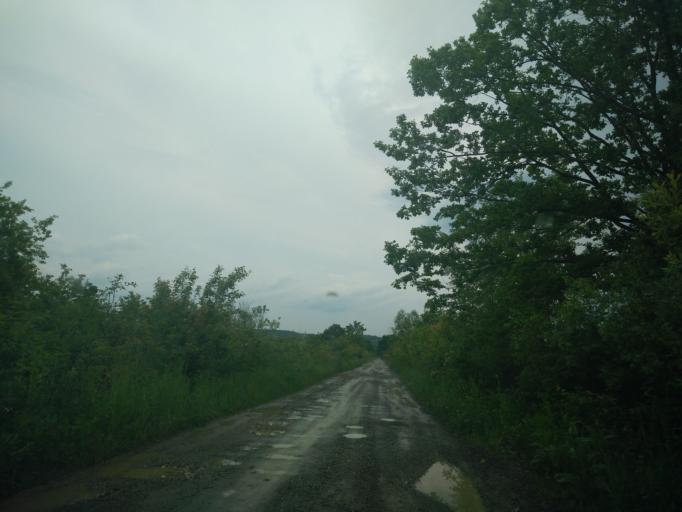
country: BA
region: Republika Srpska
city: Prijedor
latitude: 44.8921
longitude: 16.7252
